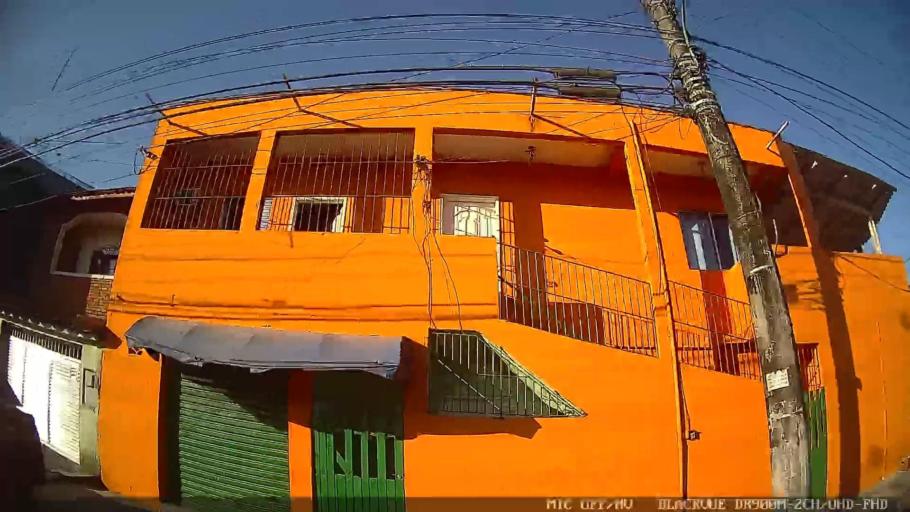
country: BR
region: Sao Paulo
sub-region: Guaruja
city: Guaruja
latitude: -23.9657
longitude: -46.2600
